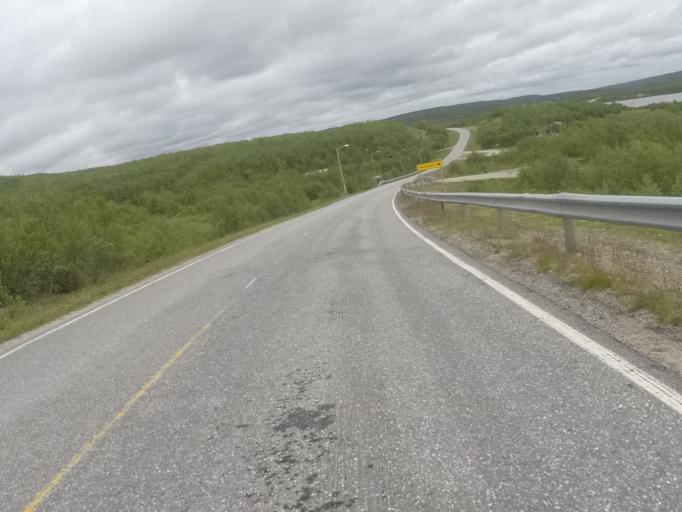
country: NO
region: Finnmark Fylke
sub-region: Kautokeino
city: Kautokeino
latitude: 69.1153
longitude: 23.2419
